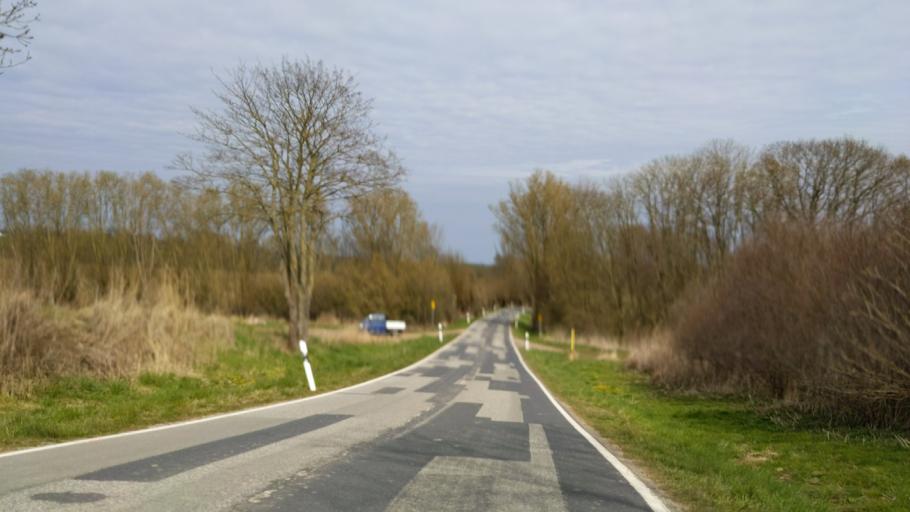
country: DE
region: Mecklenburg-Vorpommern
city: Dassow
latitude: 53.9549
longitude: 10.9570
